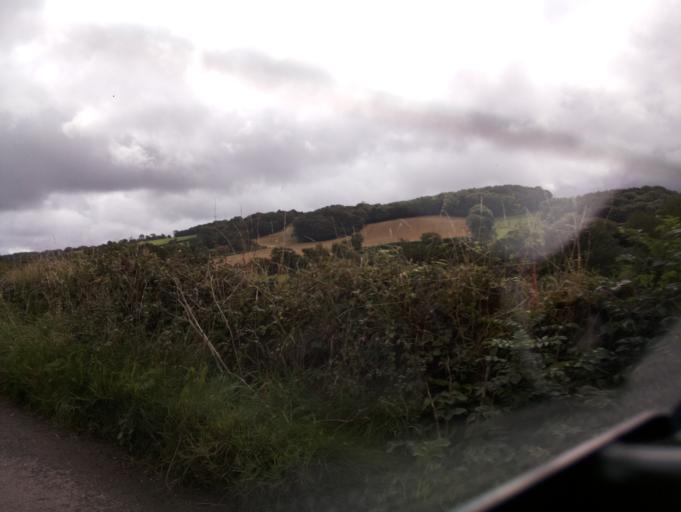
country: GB
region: England
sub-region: Devon
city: Kingsbridge
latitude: 50.2713
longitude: -3.7158
